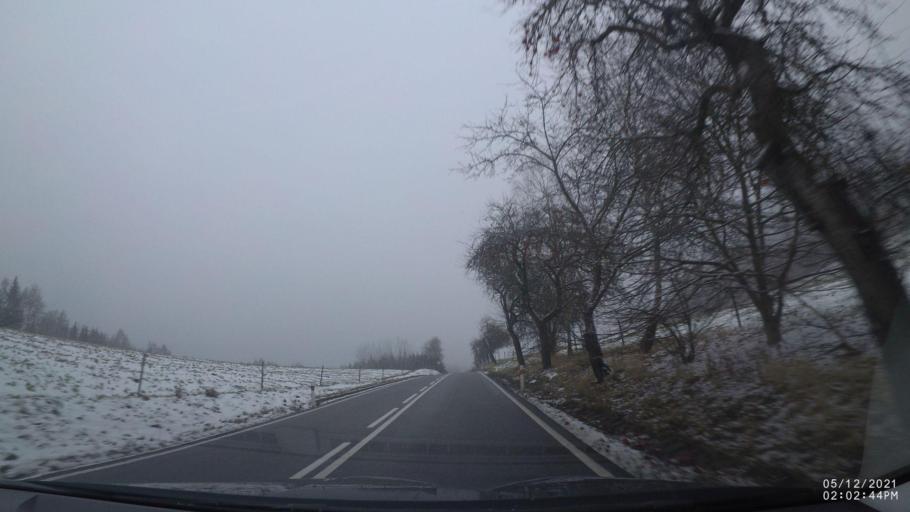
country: CZ
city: Hronov
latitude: 50.4859
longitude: 16.1403
